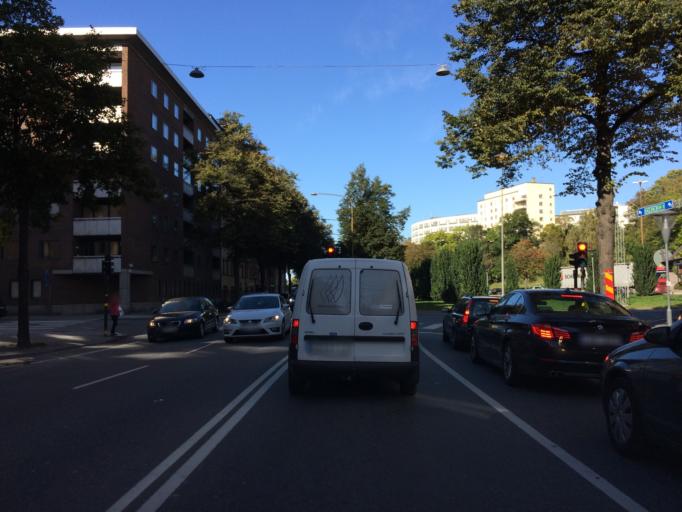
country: SE
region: Stockholm
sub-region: Stockholms Kommun
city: Stockholm
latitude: 59.3495
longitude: 18.0592
